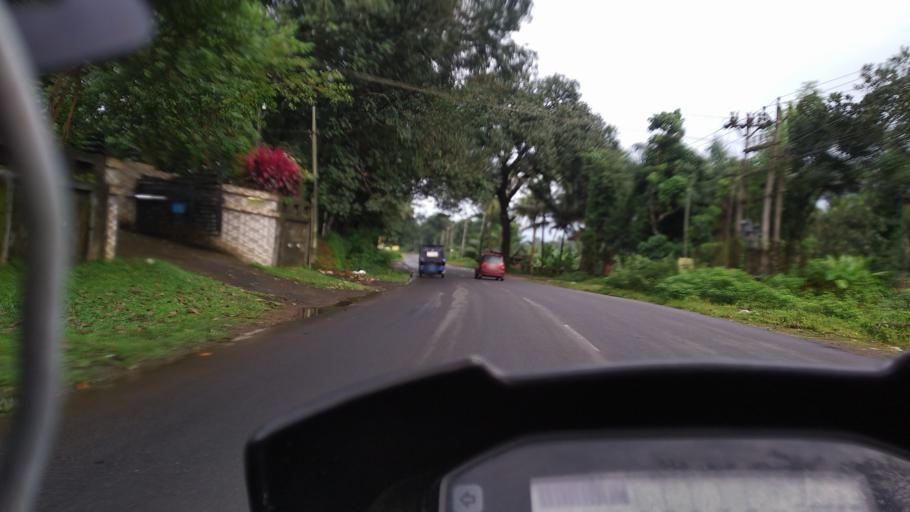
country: IN
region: Kerala
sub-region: Ernakulam
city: Kotamangalam
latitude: 10.0597
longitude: 76.6890
